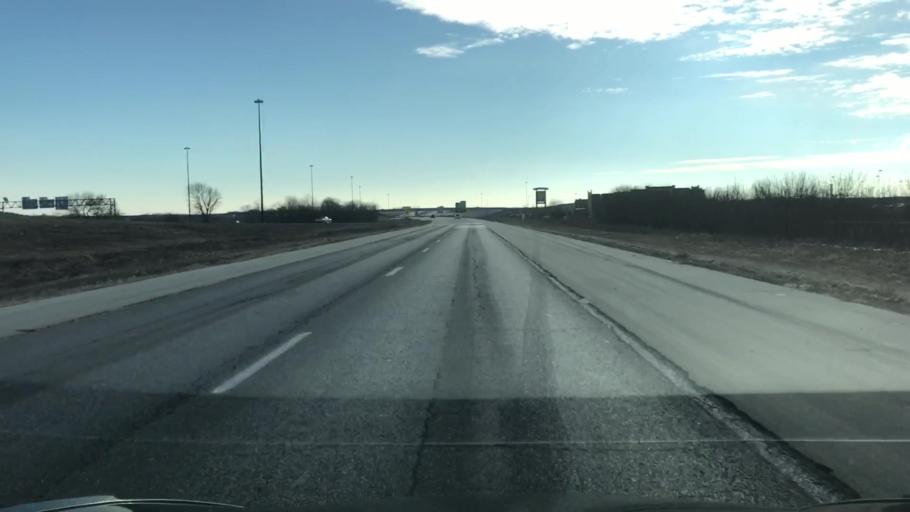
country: US
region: Iowa
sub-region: Pottawattamie County
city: Council Bluffs
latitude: 41.2273
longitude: -95.8397
